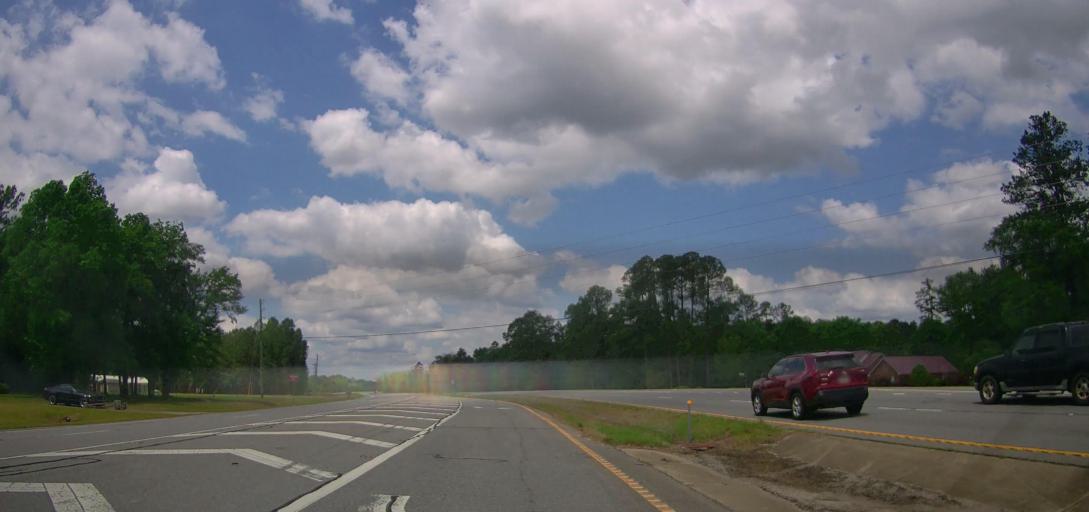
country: US
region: Georgia
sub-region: Laurens County
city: Dublin
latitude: 32.5998
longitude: -82.9666
